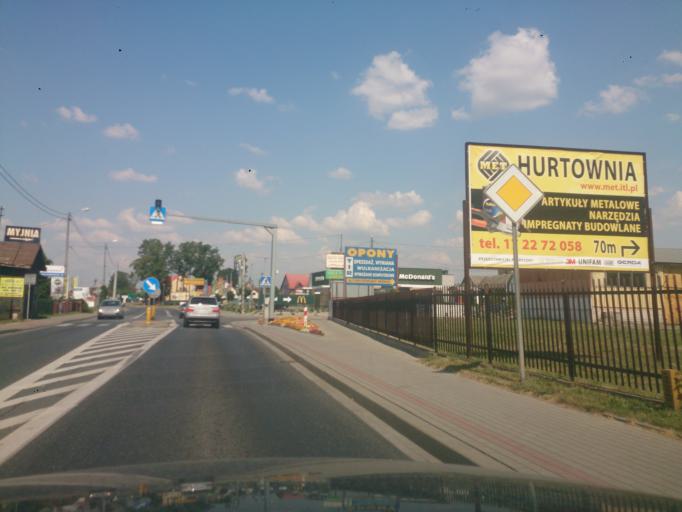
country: PL
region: Subcarpathian Voivodeship
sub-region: Powiat kolbuszowski
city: Kolbuszowa
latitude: 50.2408
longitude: 21.7798
